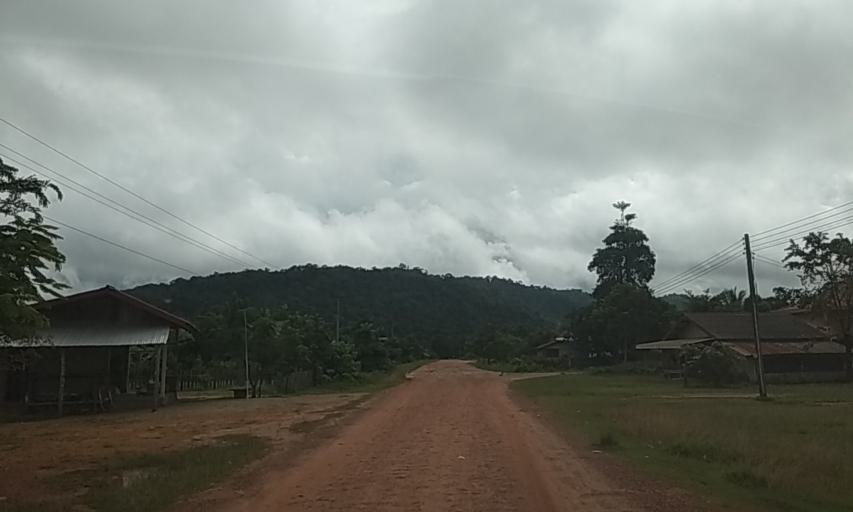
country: LA
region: Bolikhamxai
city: Bolikhan
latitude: 18.5571
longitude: 103.7380
